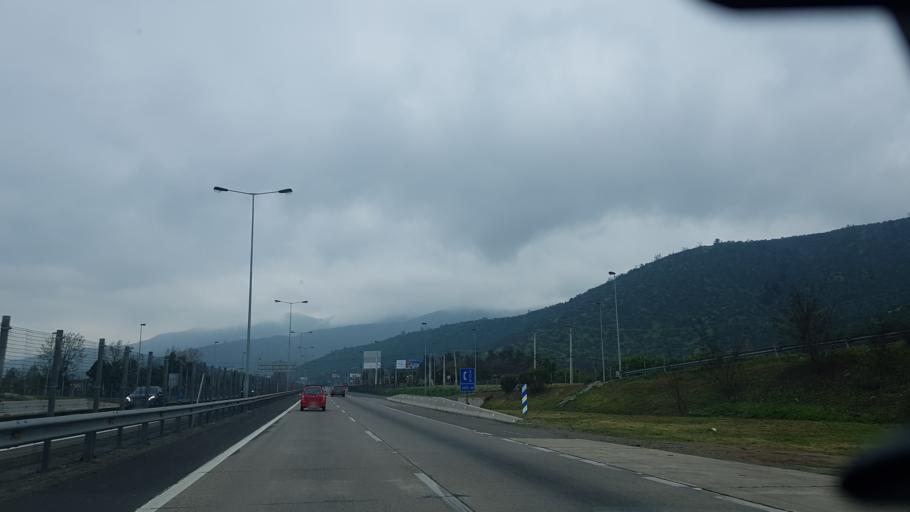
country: CL
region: Santiago Metropolitan
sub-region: Provincia de Chacabuco
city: Lampa
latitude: -33.4206
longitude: -71.0457
